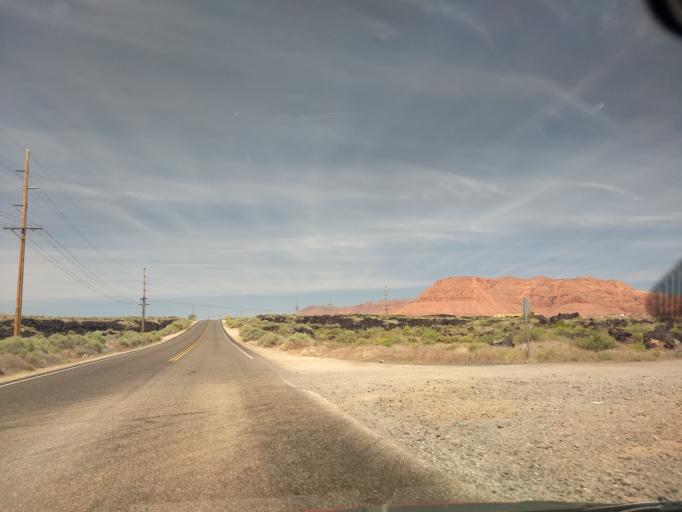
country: US
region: Utah
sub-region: Washington County
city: Santa Clara
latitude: 37.1424
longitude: -113.6439
